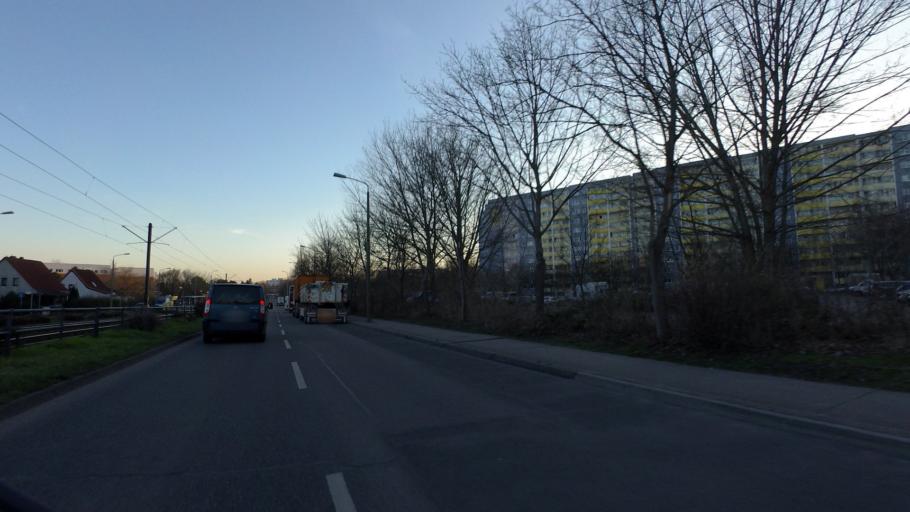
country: DE
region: Berlin
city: Marzahn
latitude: 52.5388
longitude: 13.5609
